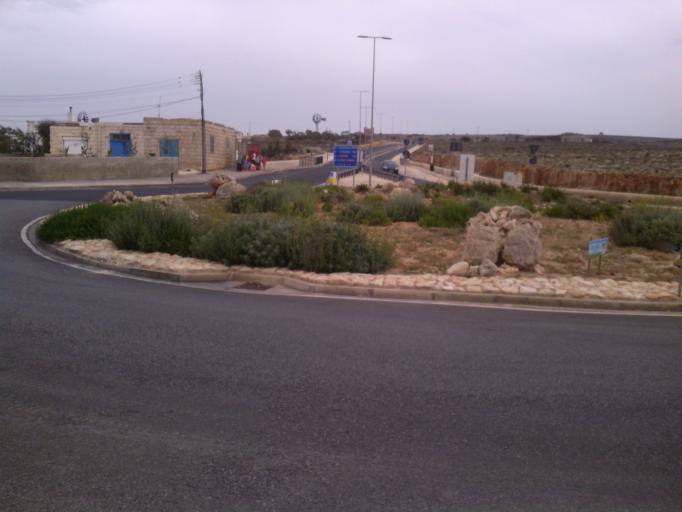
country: MT
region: Il-Mellieha
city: Mellieha
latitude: 35.9866
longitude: 14.3420
